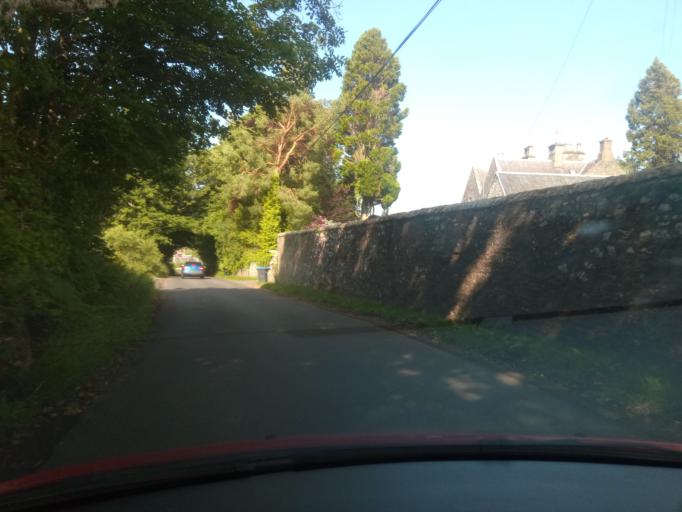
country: GB
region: Scotland
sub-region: The Scottish Borders
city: Innerleithen
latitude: 55.5076
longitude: -2.9756
